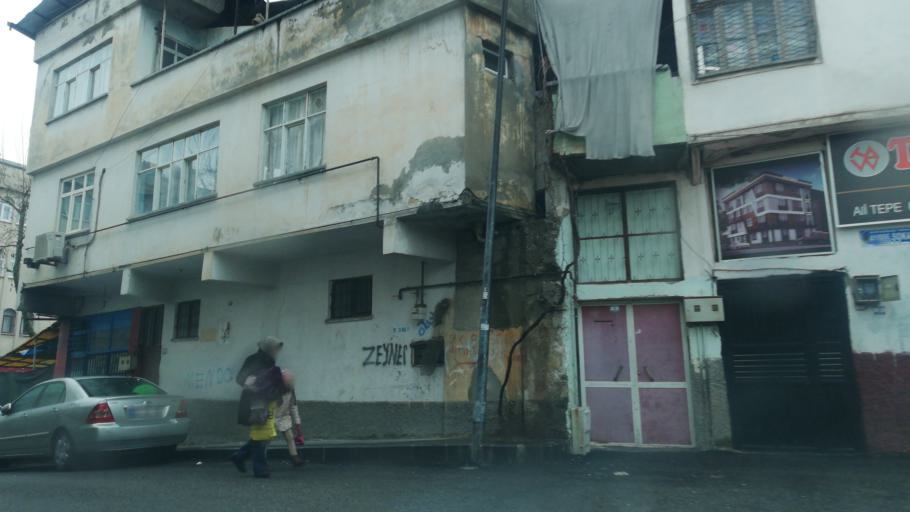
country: TR
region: Kahramanmaras
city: Kahramanmaras
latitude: 37.5884
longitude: 36.9316
